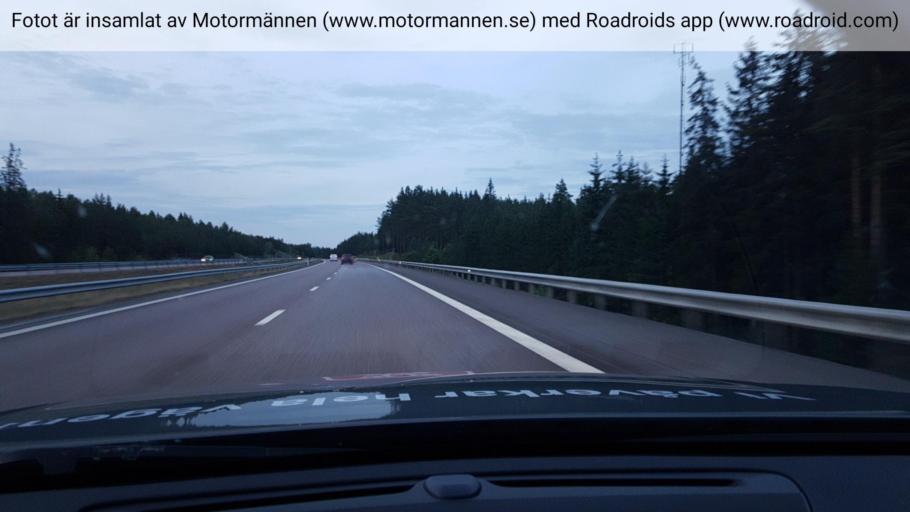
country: SE
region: Soedermanland
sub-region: Nykopings Kommun
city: Olstorp
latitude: 58.7583
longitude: 16.6724
